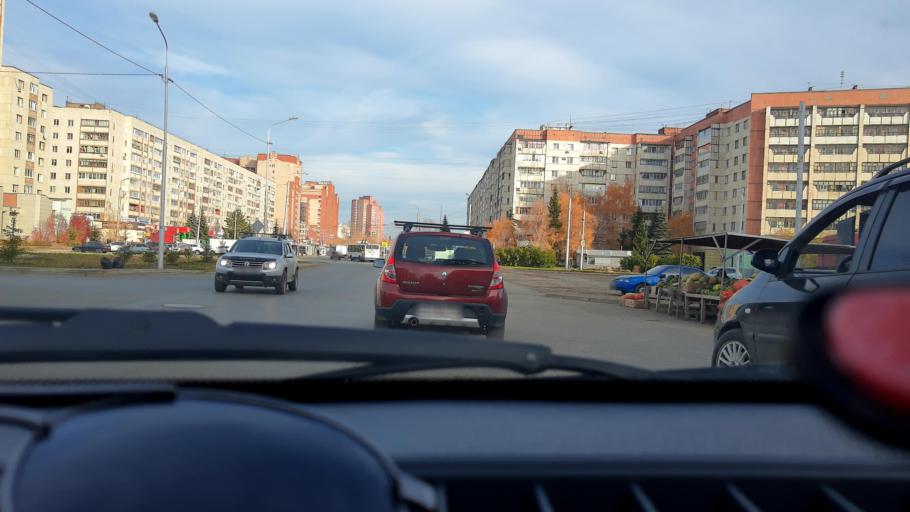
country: RU
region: Bashkortostan
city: Ufa
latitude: 54.7800
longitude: 56.1151
